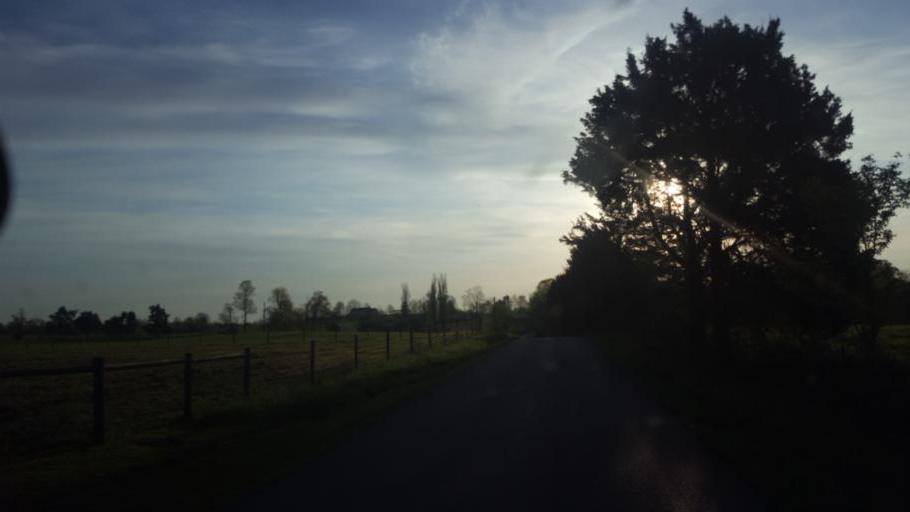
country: US
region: Kentucky
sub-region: Barren County
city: Cave City
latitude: 37.2143
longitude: -86.0070
